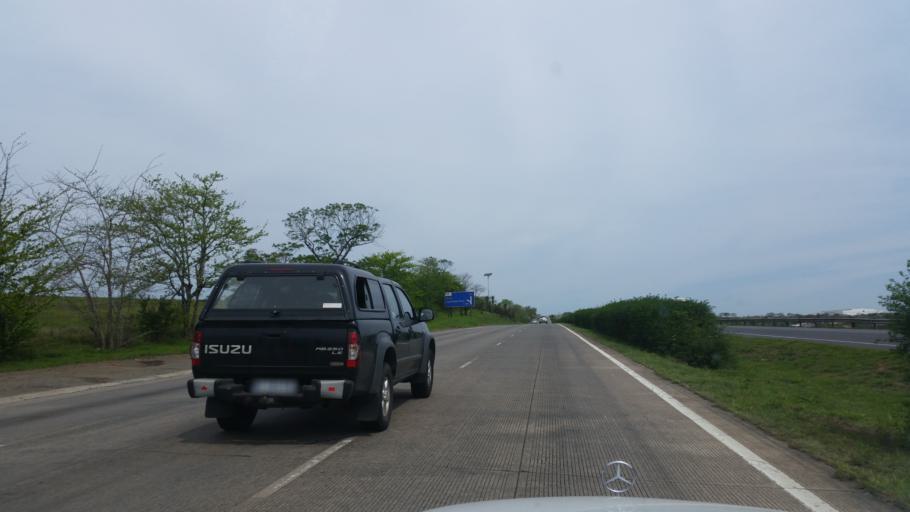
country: ZA
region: KwaZulu-Natal
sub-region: uMgungundlovu District Municipality
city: Camperdown
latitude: -29.6792
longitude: 30.4717
